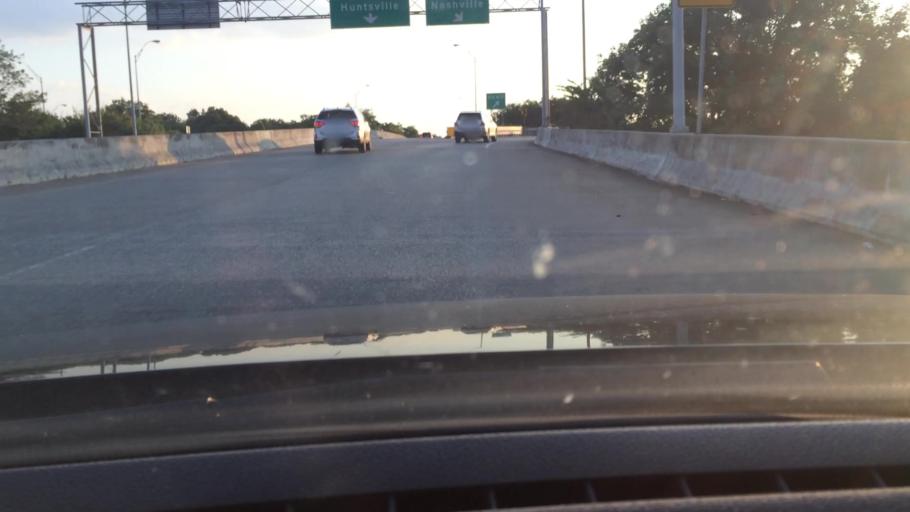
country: US
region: Tennessee
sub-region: Davidson County
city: Oak Hill
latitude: 36.1022
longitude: -86.7636
